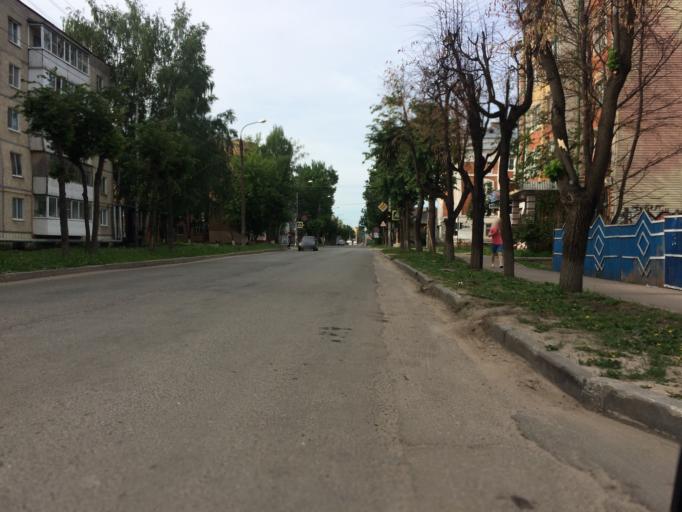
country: RU
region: Mariy-El
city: Yoshkar-Ola
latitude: 56.6423
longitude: 47.9025
